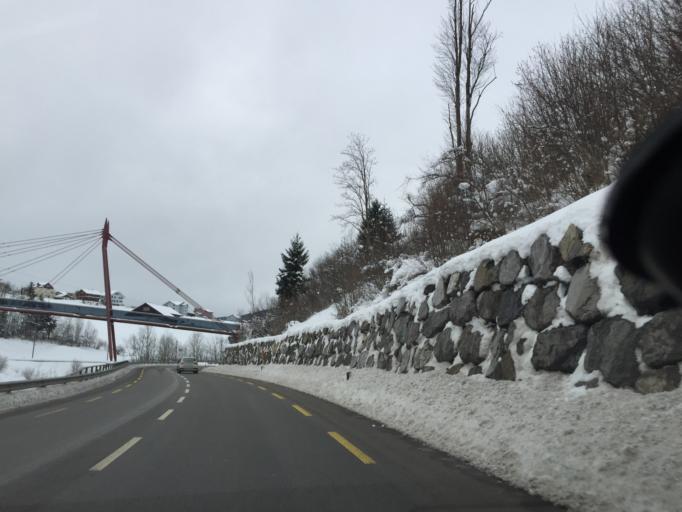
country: CH
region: Schwyz
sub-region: Bezirk Einsiedeln
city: Einsiedeln
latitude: 47.1503
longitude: 8.7347
